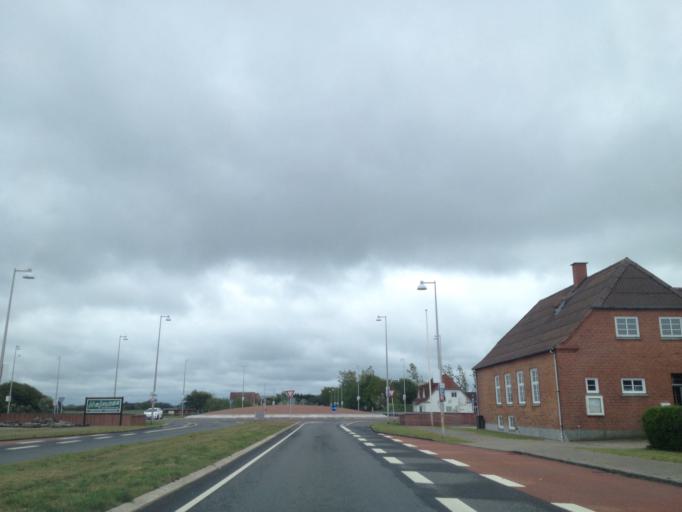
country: DK
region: South Denmark
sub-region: Tonder Kommune
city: Tonder
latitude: 55.0152
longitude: 8.8458
